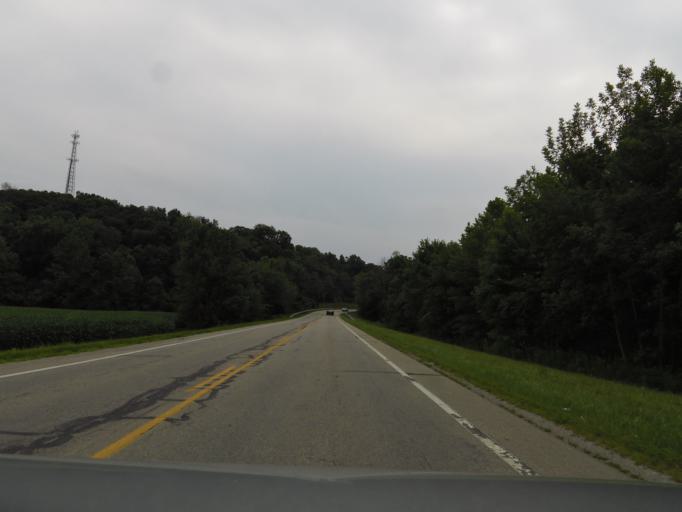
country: US
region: Ohio
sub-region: Brown County
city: Mount Orab
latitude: 38.9499
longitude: -83.9082
